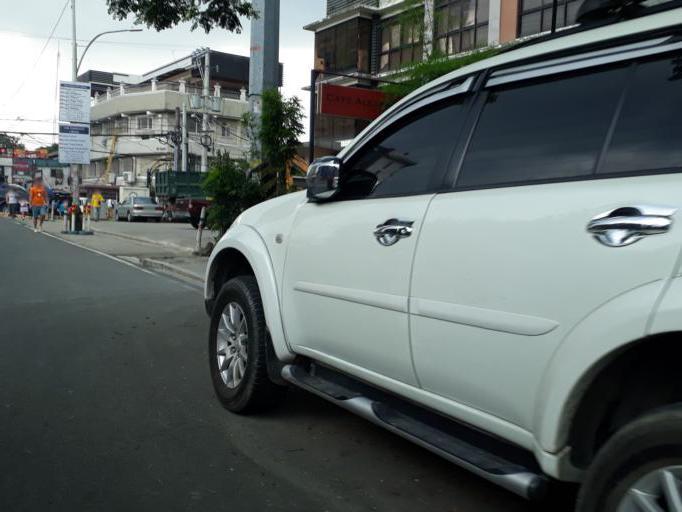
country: PH
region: Calabarzon
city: Bagong Pagasa
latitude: 14.6700
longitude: 121.0528
